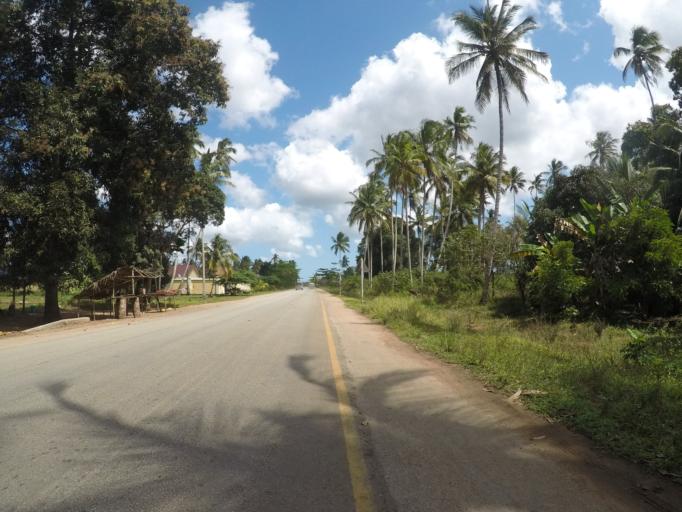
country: TZ
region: Zanzibar Central/South
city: Koani
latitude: -6.1546
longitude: 39.3296
